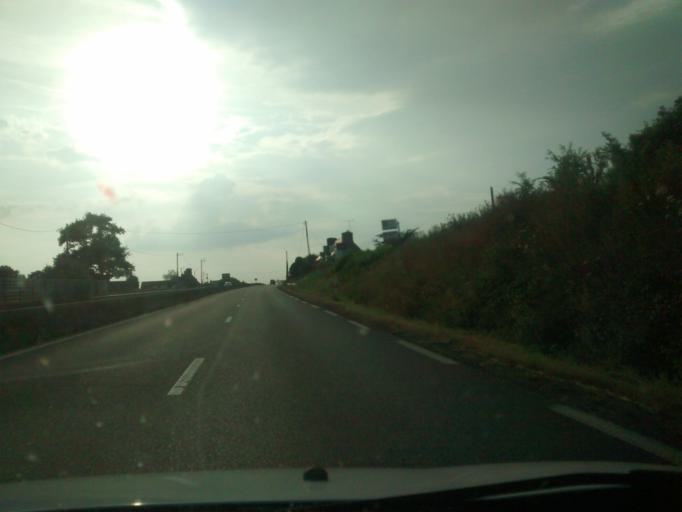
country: FR
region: Brittany
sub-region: Departement des Cotes-d'Armor
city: Ploubezre
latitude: 48.7216
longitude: -3.4232
